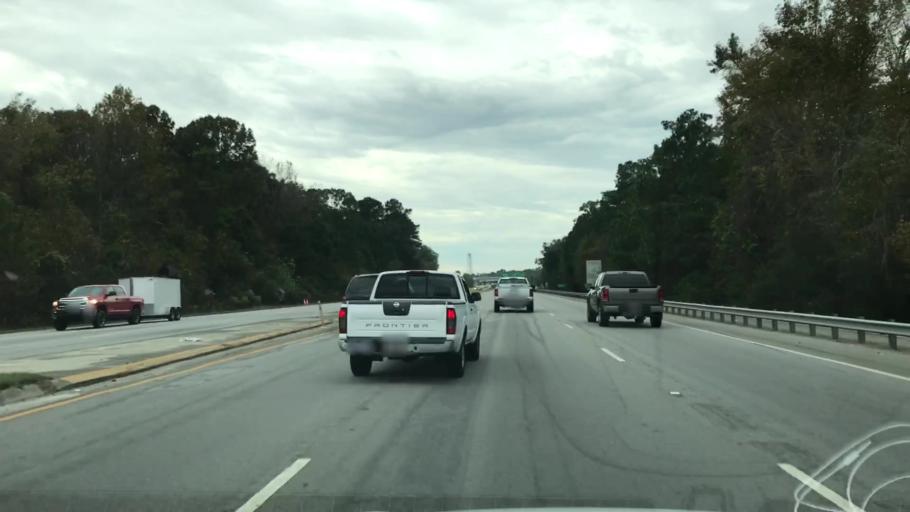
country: US
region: South Carolina
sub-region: Berkeley County
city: Goose Creek
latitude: 32.9826
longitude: -80.0424
